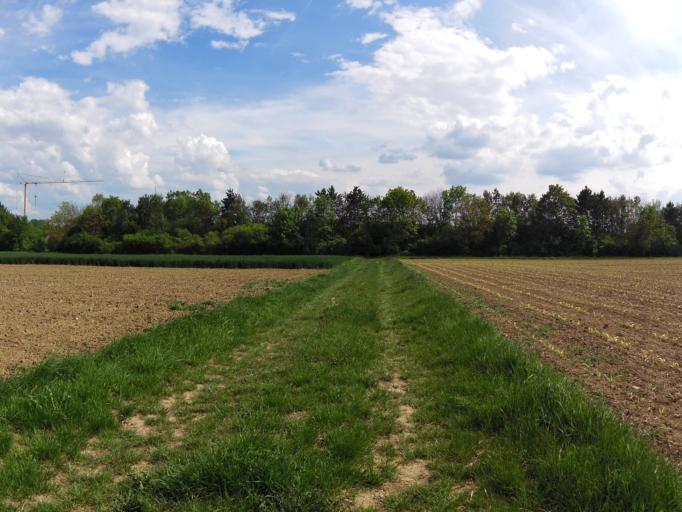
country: DE
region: Bavaria
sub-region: Regierungsbezirk Unterfranken
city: Theilheim
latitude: 49.7345
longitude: 10.0233
